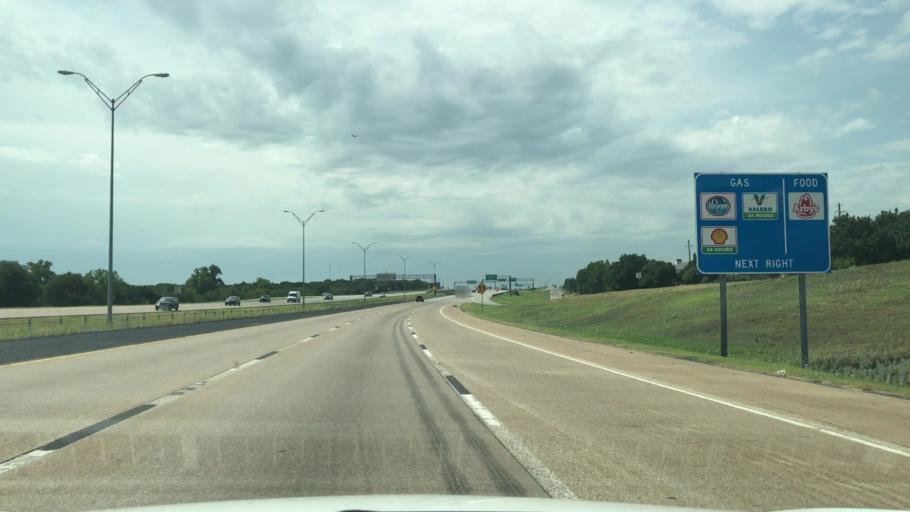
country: US
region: Texas
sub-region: Tarrant County
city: Euless
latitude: 32.8651
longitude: -97.0649
